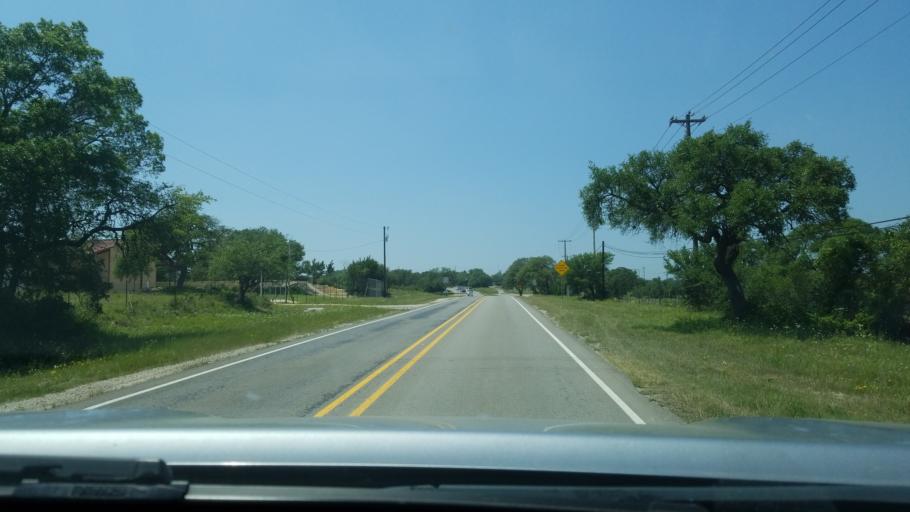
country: US
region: Texas
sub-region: Blanco County
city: Blanco
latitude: 30.0696
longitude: -98.4055
